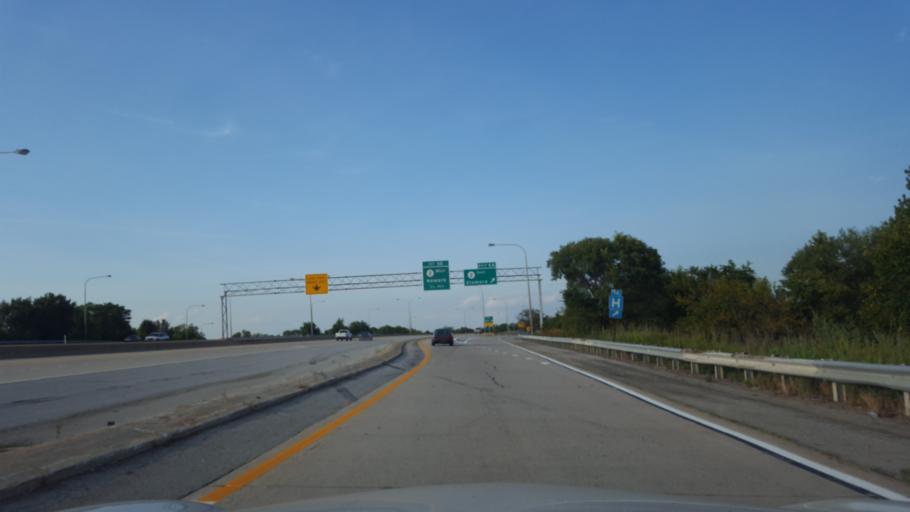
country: US
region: Delaware
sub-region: New Castle County
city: Elsmere
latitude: 39.7345
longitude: -75.6210
